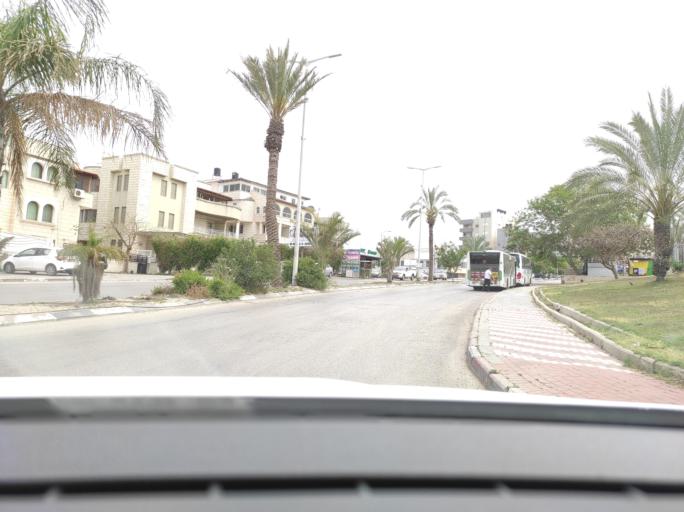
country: IL
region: Central District
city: Kafr Qasim
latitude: 32.1183
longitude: 34.9660
